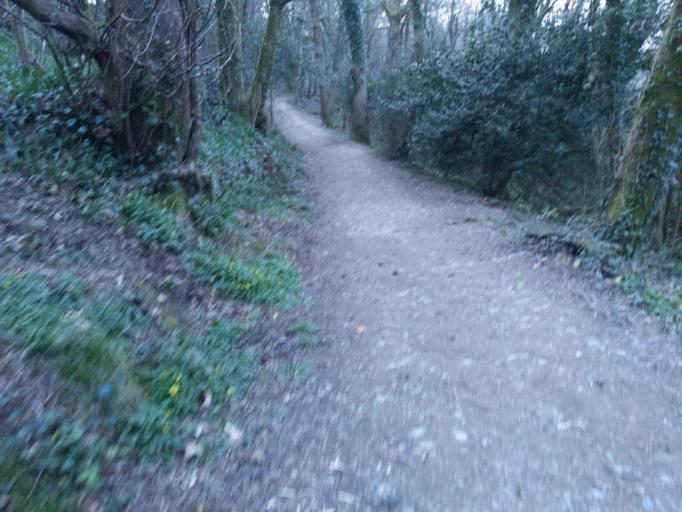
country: GB
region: England
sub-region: Plymouth
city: Plymouth
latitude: 50.4188
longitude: -4.1409
